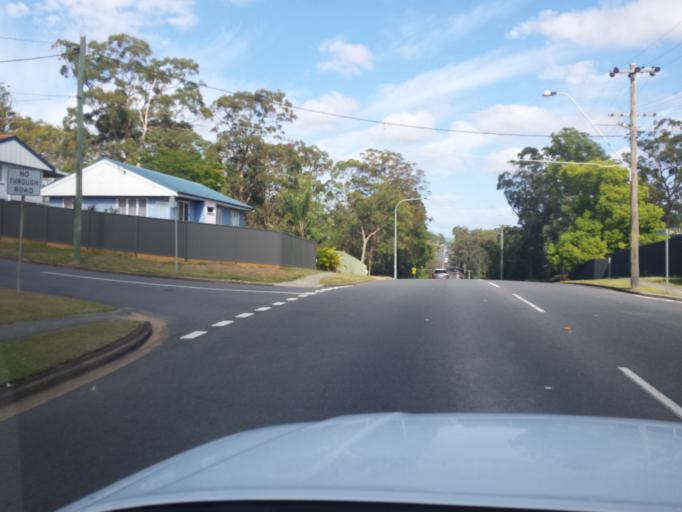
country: AU
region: Queensland
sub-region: Brisbane
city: Stafford Heights
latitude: -27.3906
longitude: 153.0078
